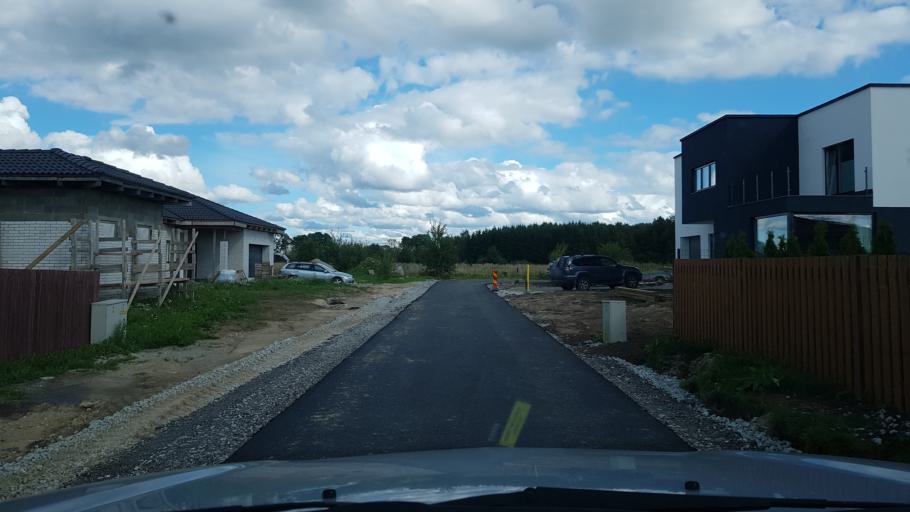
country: EE
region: Harju
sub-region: Rae vald
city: Jueri
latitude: 59.3759
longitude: 24.8326
